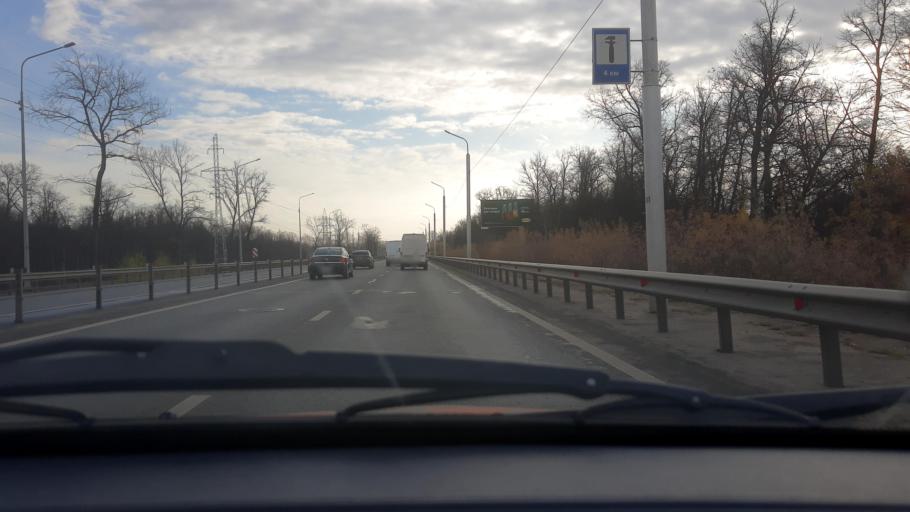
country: RU
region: Bashkortostan
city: Ufa
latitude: 54.6992
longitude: 55.8828
